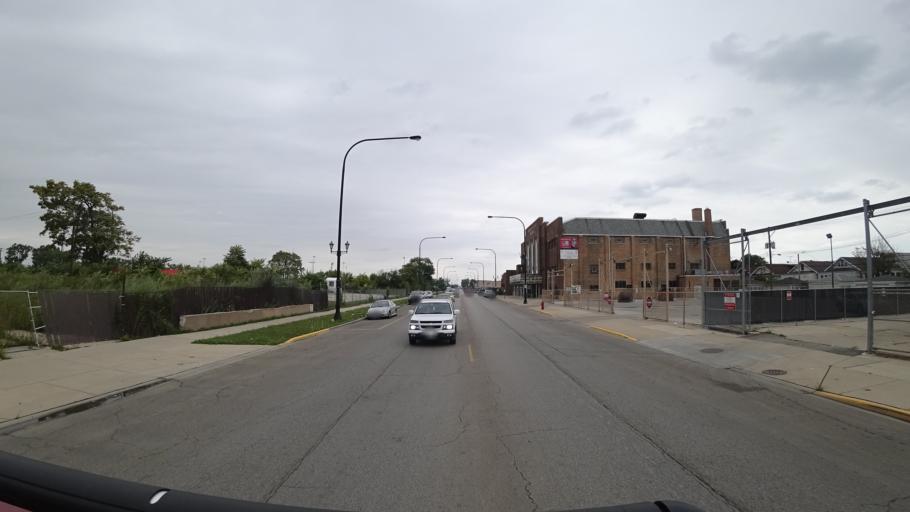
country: US
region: Illinois
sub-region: Cook County
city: Cicero
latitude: 41.8536
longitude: -87.7542
